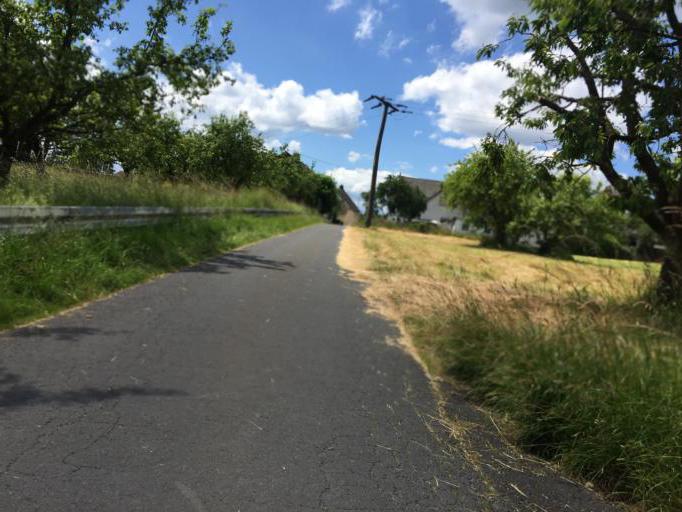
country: DE
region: Rheinland-Pfalz
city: Girod
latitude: 50.4459
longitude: 7.9086
